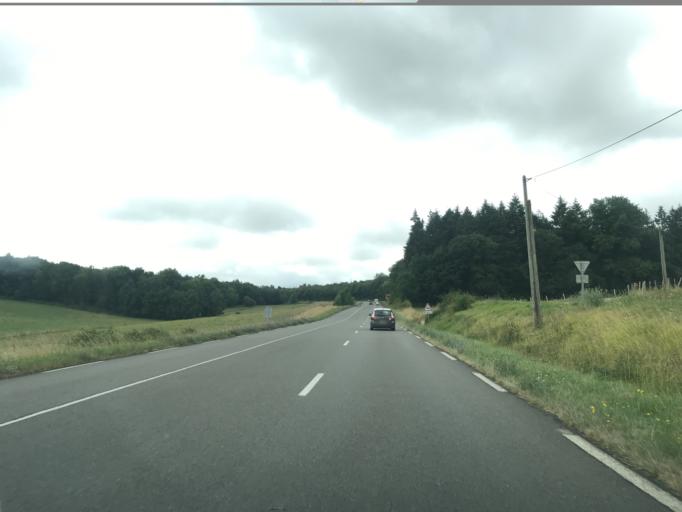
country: FR
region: Poitou-Charentes
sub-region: Departement de la Charente
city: Dignac
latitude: 45.5500
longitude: 0.2745
